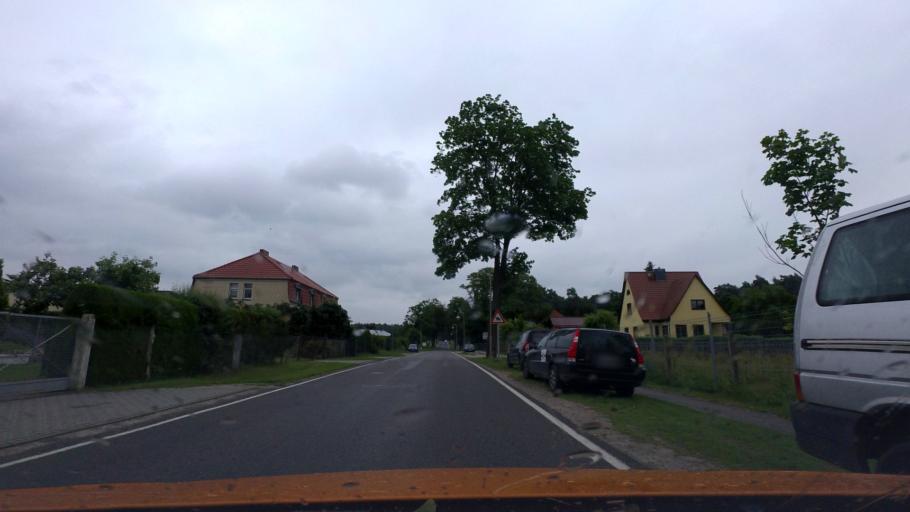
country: DE
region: Brandenburg
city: Strausberg
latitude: 52.6051
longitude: 13.8748
